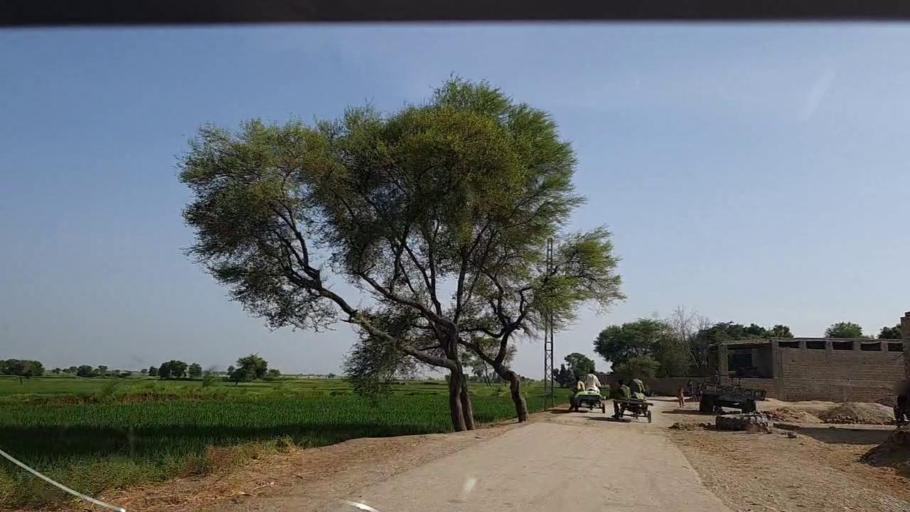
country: PK
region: Sindh
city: Khairpur Nathan Shah
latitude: 27.0050
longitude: 67.6710
